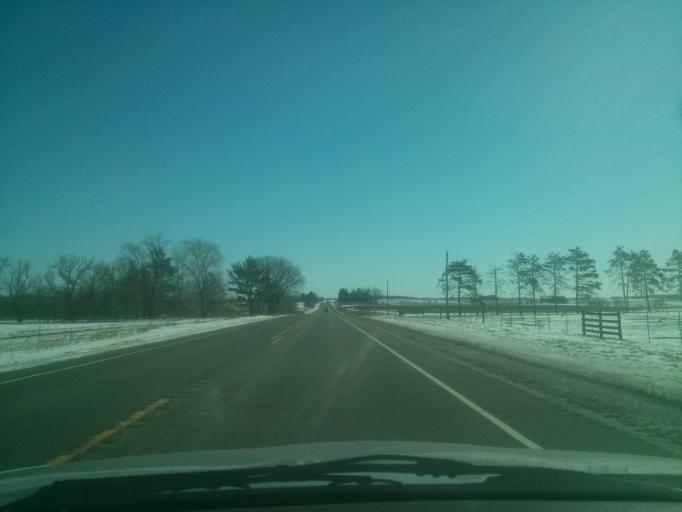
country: US
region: Wisconsin
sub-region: Polk County
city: Clear Lake
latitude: 45.1364
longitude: -92.3501
